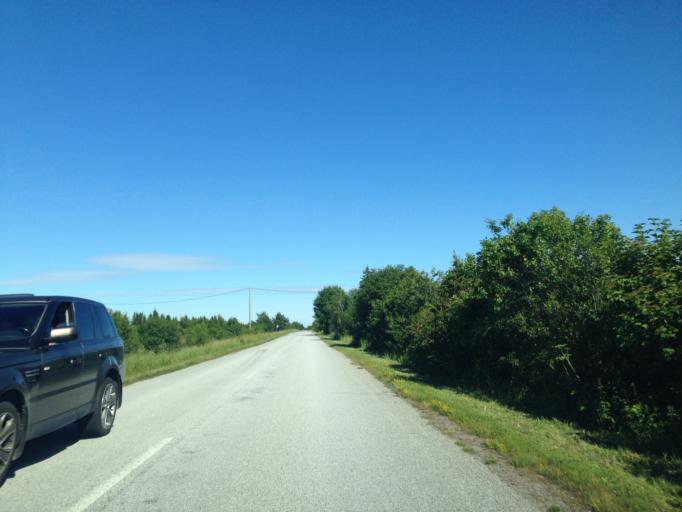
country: EE
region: Harju
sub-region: Anija vald
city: Kehra
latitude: 59.4688
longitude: 25.2783
